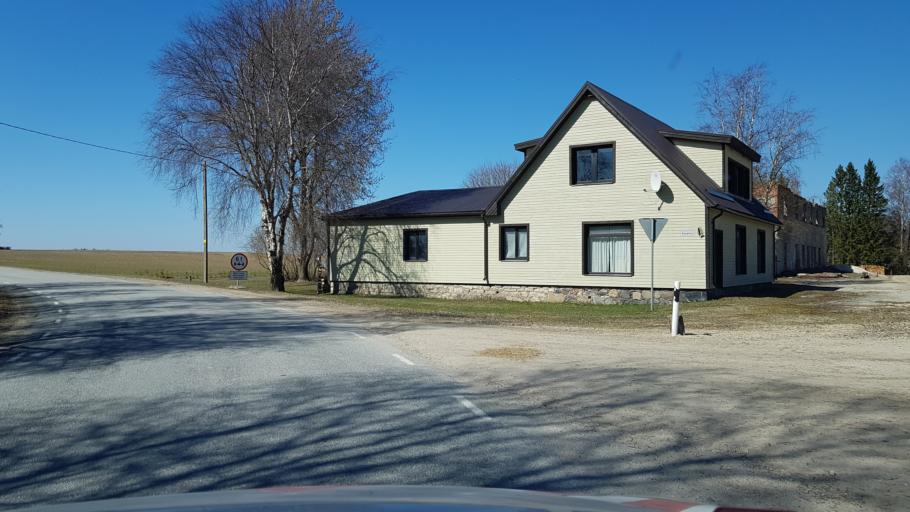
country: EE
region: Jaervamaa
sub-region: Koeru vald
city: Koeru
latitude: 59.0519
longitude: 26.0874
